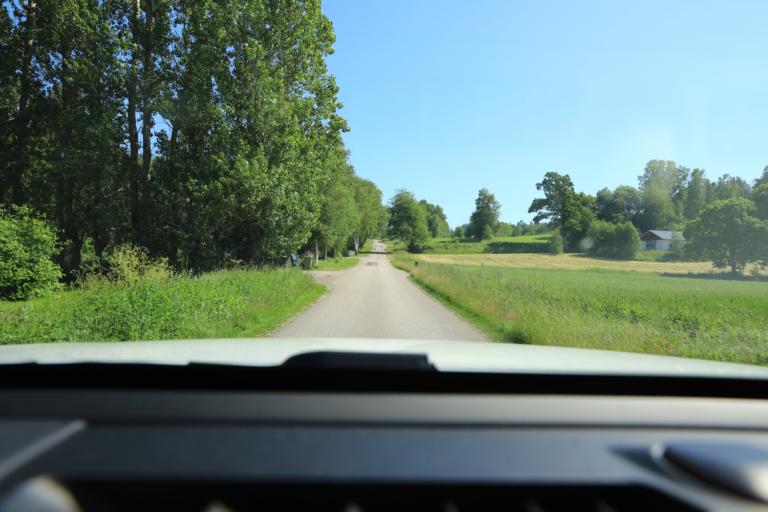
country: SE
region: Halland
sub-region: Varbergs Kommun
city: Veddige
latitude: 57.1988
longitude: 12.3209
